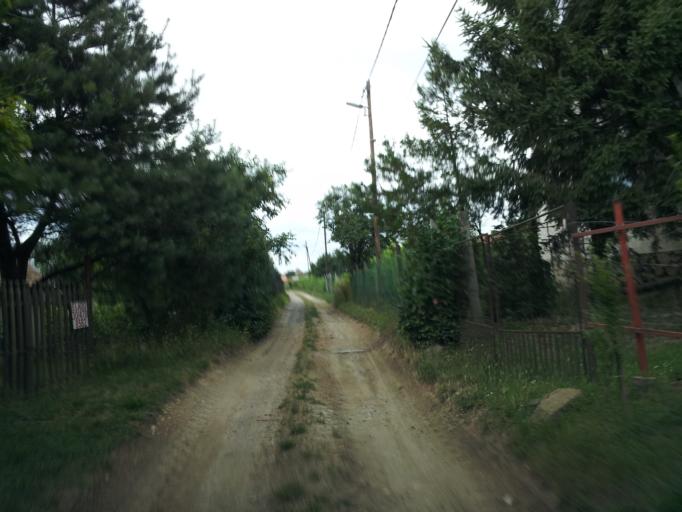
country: HU
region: Veszprem
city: Devecser
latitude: 47.1346
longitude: 17.3668
